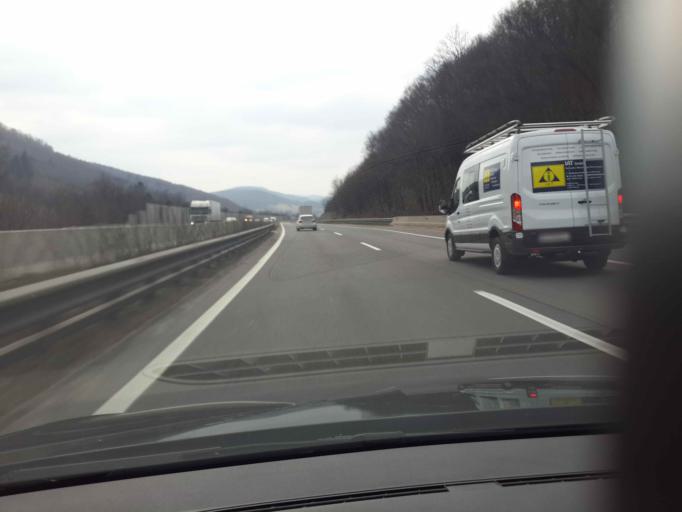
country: AT
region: Lower Austria
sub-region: Politischer Bezirk Baden
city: Klausen-Leopoldsdorf
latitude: 48.0815
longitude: 16.0453
